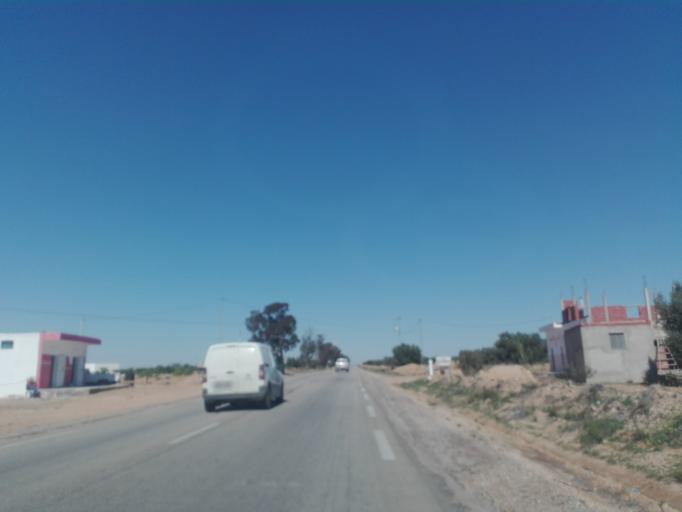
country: TN
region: Safaqis
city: Bi'r `Ali Bin Khalifah
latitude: 34.7531
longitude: 10.3389
